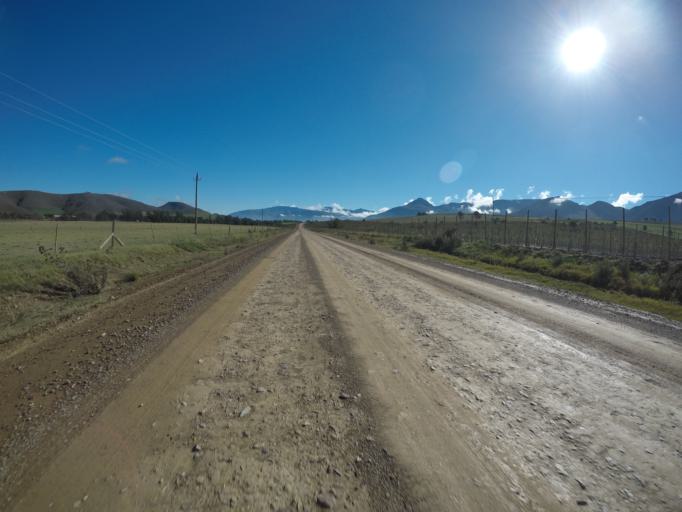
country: ZA
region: Western Cape
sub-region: Overberg District Municipality
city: Caledon
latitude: -34.0870
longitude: 19.6548
